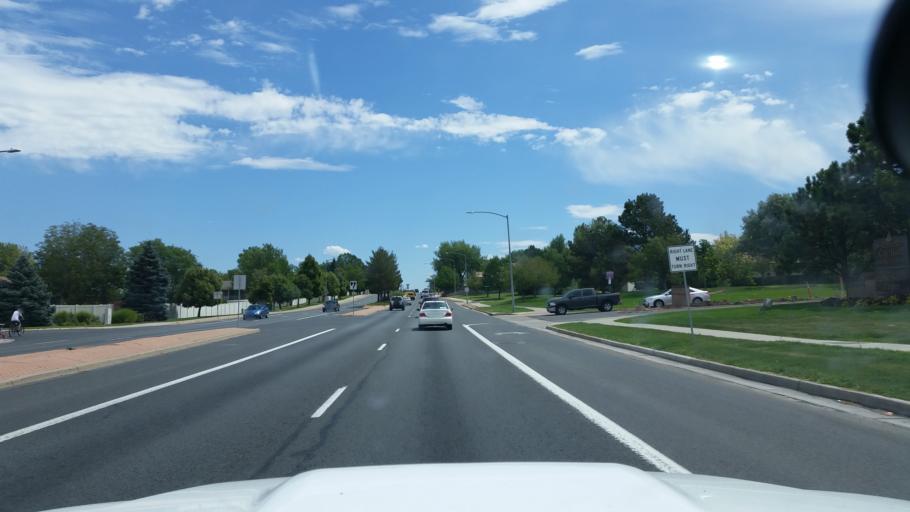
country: US
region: Colorado
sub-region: Adams County
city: Westminster
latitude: 39.8635
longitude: -105.0481
